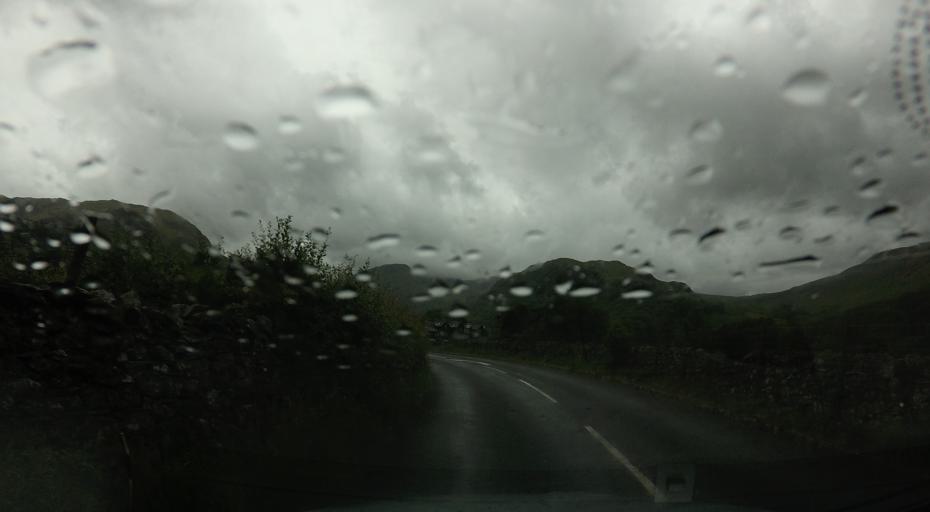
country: GB
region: England
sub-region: Cumbria
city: Keswick
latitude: 54.5143
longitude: -3.1561
